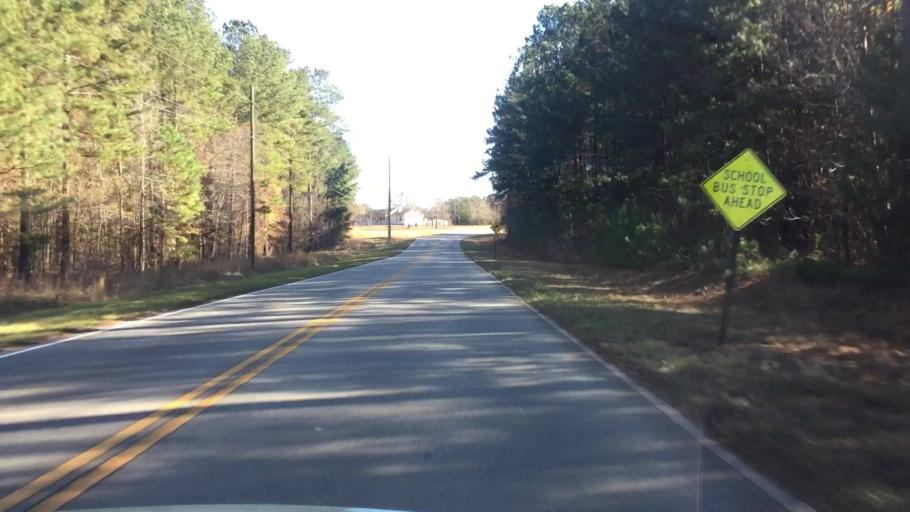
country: US
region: Georgia
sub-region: Newton County
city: Oakwood
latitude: 33.4789
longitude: -84.0372
